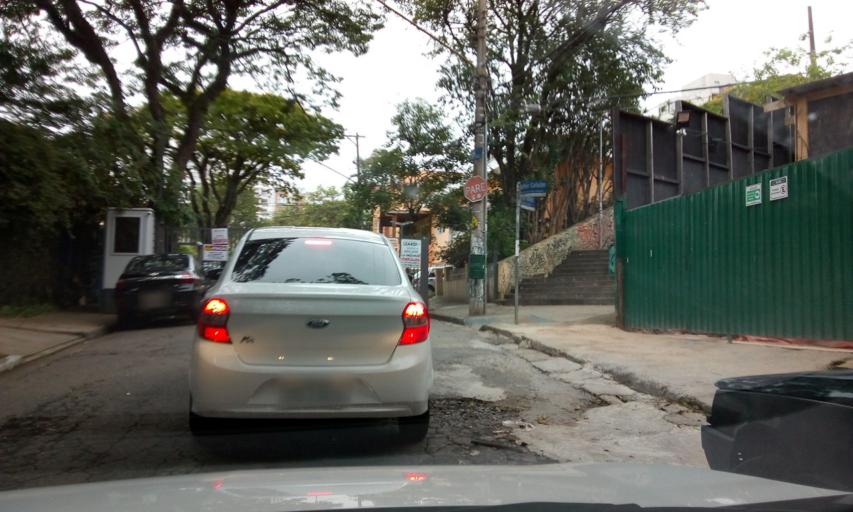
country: BR
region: Sao Paulo
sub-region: Sao Paulo
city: Sao Paulo
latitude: -23.5479
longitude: -46.6911
